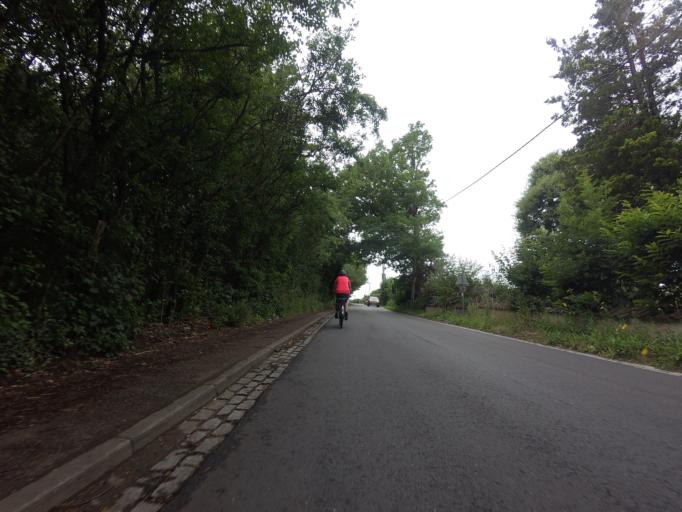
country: GB
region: England
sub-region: Kent
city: Kings Hill
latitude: 51.2931
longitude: 0.3687
